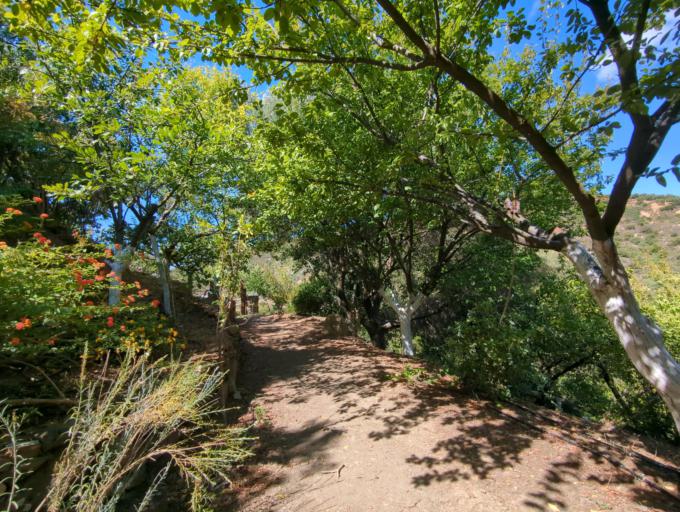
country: GR
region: Crete
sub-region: Nomos Chanias
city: Galatas
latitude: 35.4197
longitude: 23.9389
